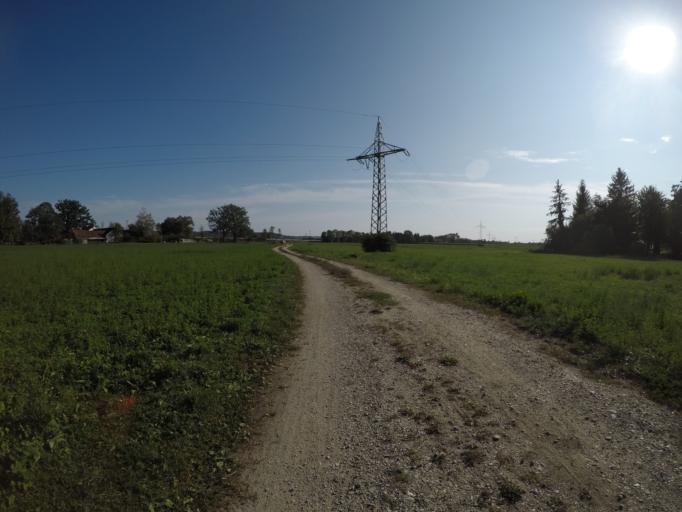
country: DE
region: Bavaria
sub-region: Lower Bavaria
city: Bruckberg
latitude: 48.4922
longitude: 11.9969
